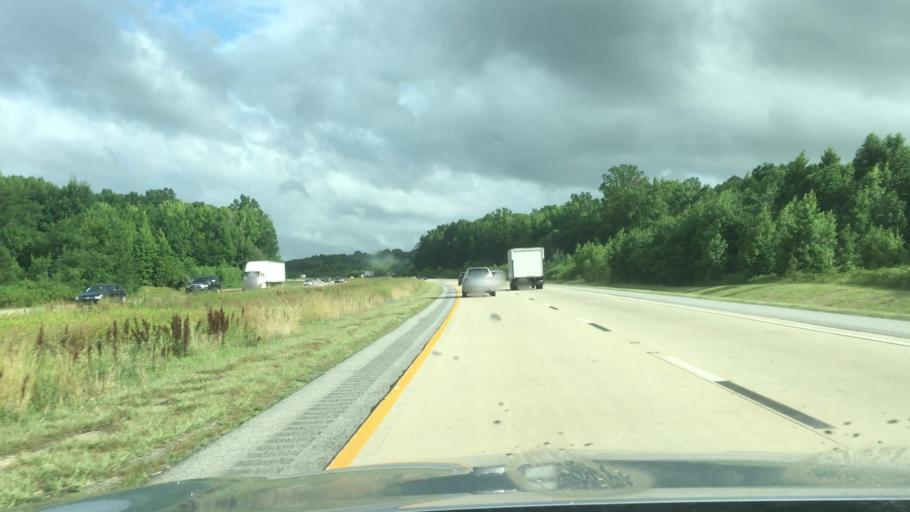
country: US
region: Delaware
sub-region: New Castle County
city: Townsend
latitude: 39.3615
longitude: -75.6542
